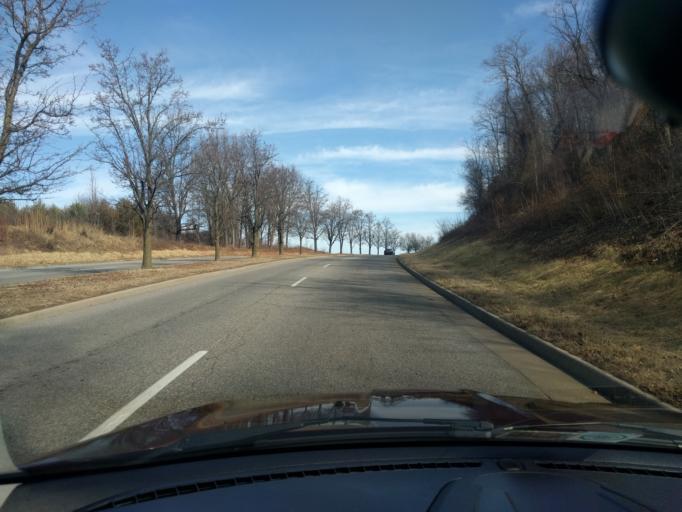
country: US
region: Virginia
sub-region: City of Staunton
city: Staunton
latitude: 38.1419
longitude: -79.0641
